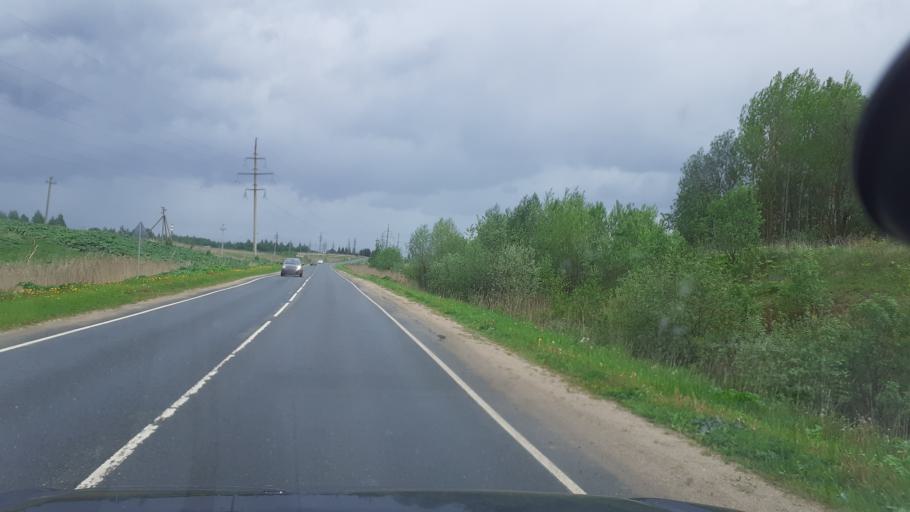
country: RU
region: Moskovskaya
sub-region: Volokolamskiy Rayon
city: Volokolamsk
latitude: 56.0204
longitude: 35.9440
